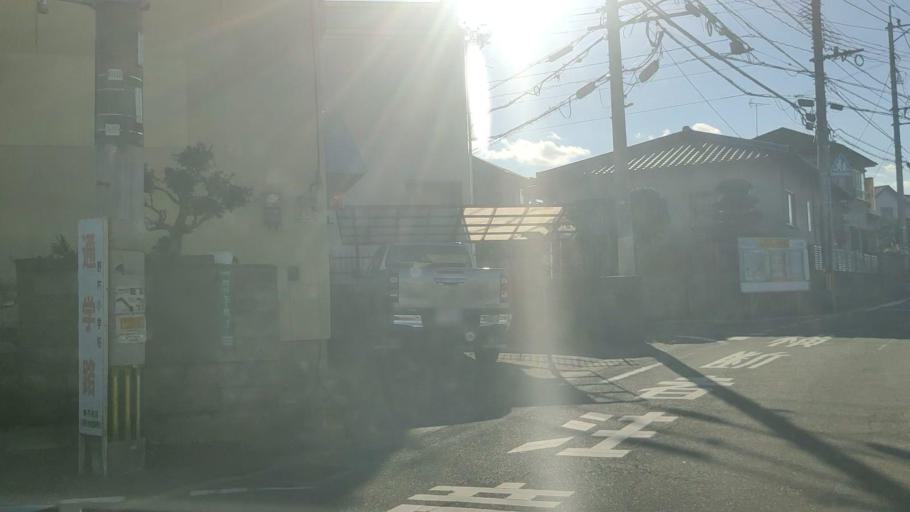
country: JP
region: Fukuoka
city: Fukuoka-shi
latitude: 33.5420
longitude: 130.3539
